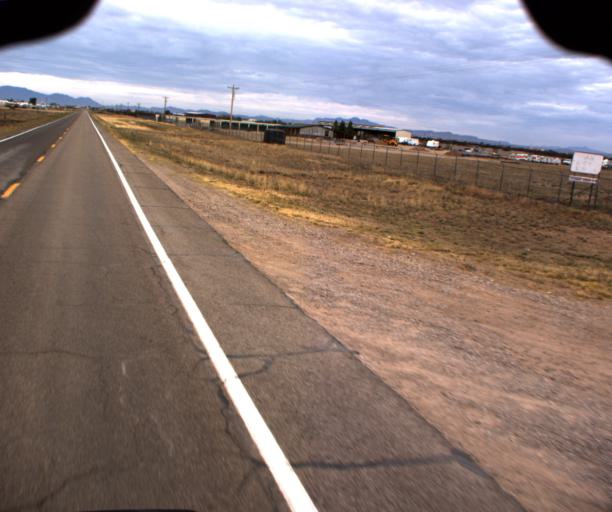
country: US
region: Arizona
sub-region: Cochise County
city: Willcox
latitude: 32.2794
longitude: -109.8139
